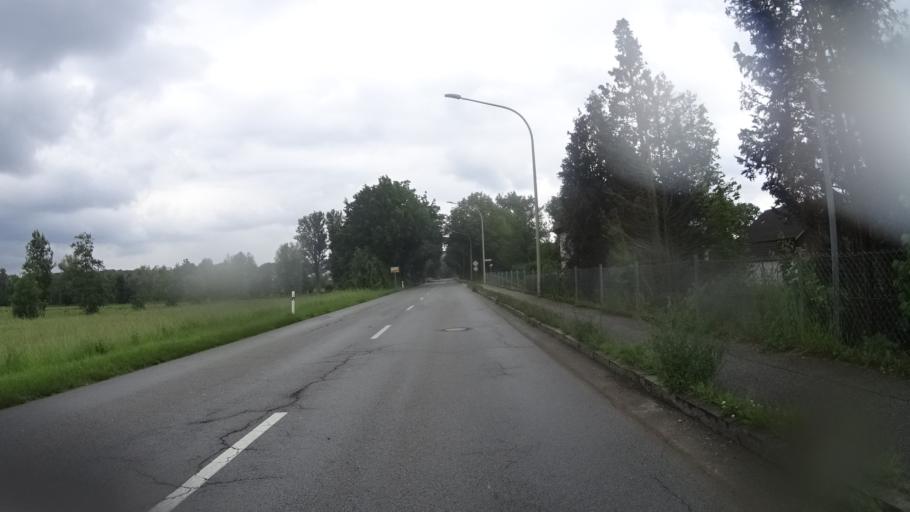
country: DE
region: Bavaria
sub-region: Lower Bavaria
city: Hebertsfelden
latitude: 48.4140
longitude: 12.8170
